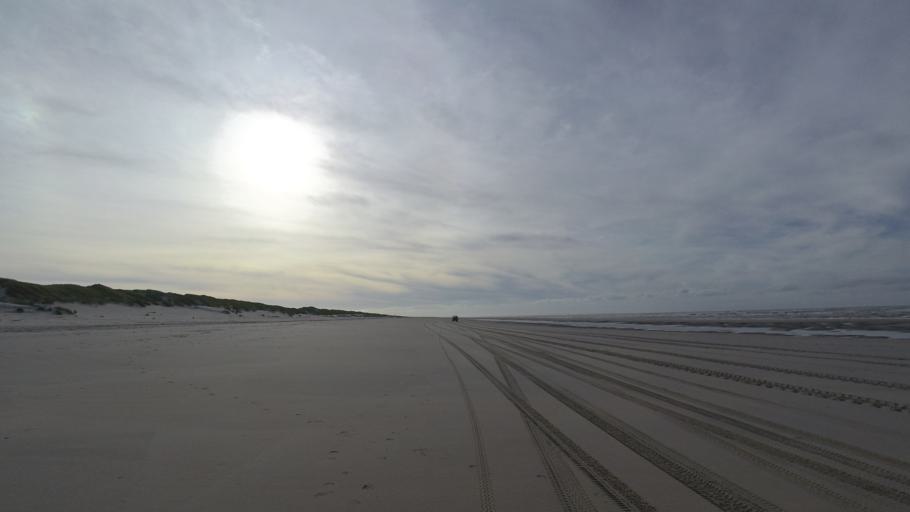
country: NL
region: Friesland
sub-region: Gemeente Ameland
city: Nes
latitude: 53.4644
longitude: 5.8423
